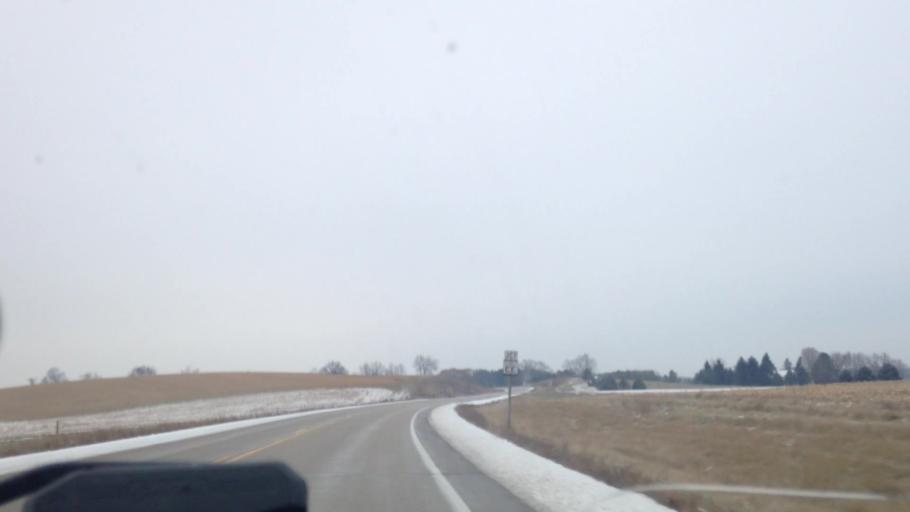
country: US
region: Wisconsin
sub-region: Jefferson County
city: Ixonia
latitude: 43.2368
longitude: -88.5185
